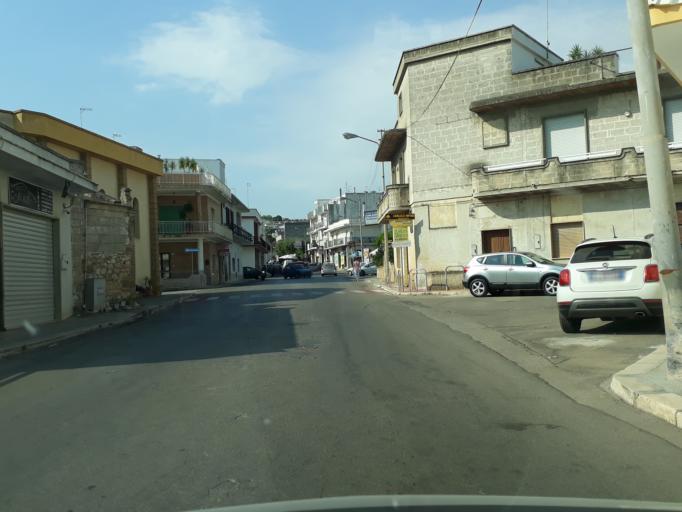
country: IT
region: Apulia
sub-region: Provincia di Brindisi
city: Carovigno
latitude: 40.7124
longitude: 17.6596
